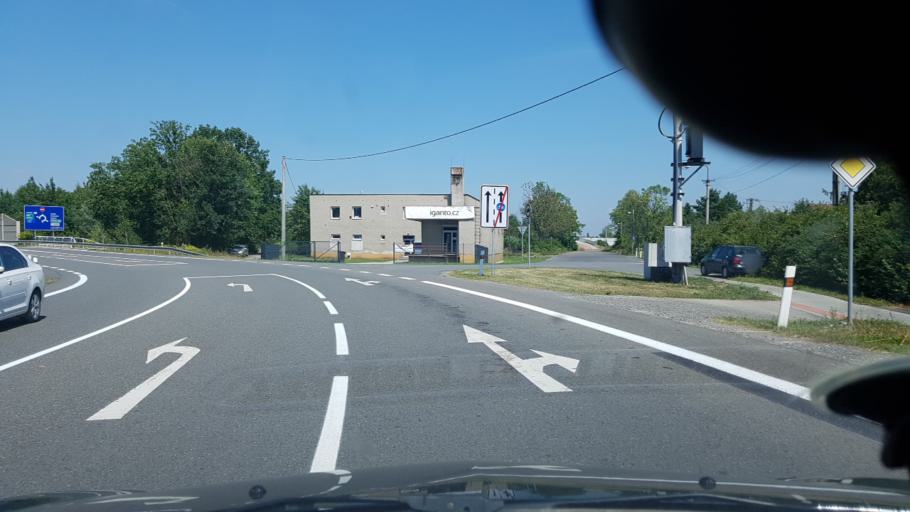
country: CZ
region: Moravskoslezsky
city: Stary Bohumin
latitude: 49.9090
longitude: 18.3377
